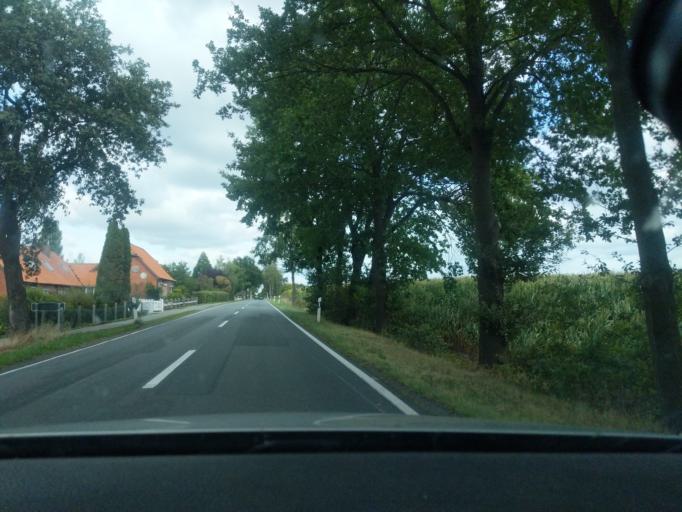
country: DE
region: Lower Saxony
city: Warpe
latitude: 52.7466
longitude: 9.0712
